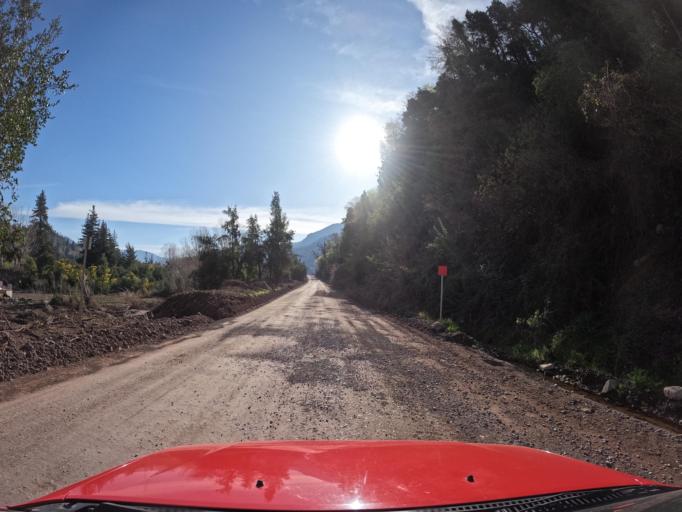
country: CL
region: O'Higgins
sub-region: Provincia de Colchagua
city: Chimbarongo
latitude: -34.9976
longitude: -70.8080
